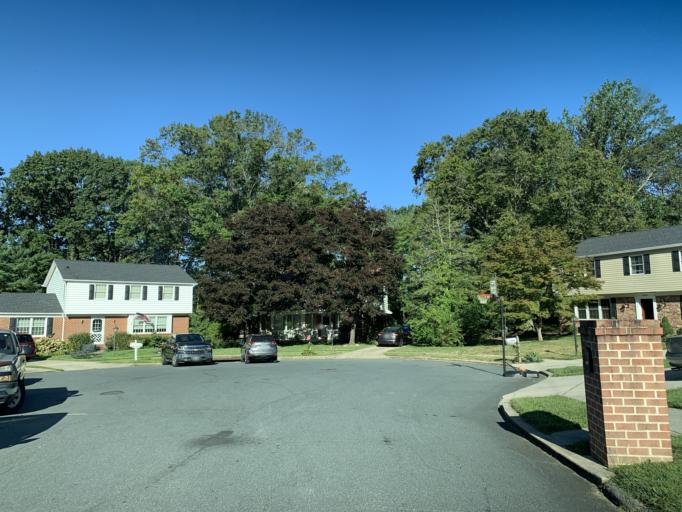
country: US
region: Maryland
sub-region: Harford County
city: Bel Air North
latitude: 39.5507
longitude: -76.3769
